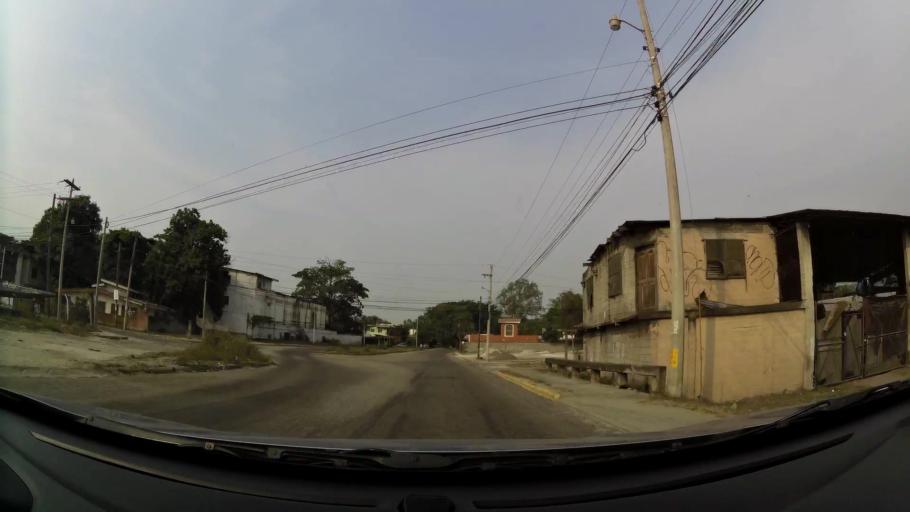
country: HN
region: Cortes
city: San Pedro Sula
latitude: 15.5402
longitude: -88.0083
